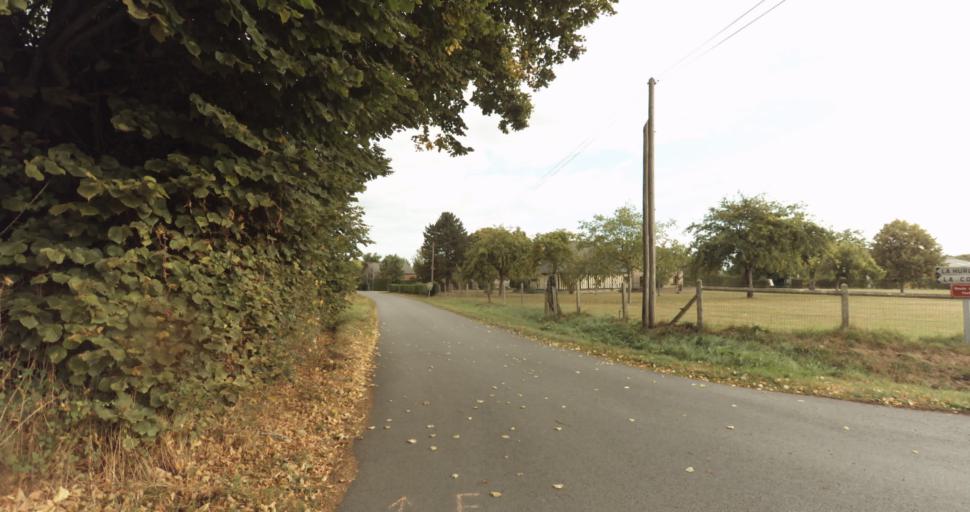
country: FR
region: Lower Normandy
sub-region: Departement de l'Orne
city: Vimoutiers
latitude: 48.9486
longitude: 0.2516
